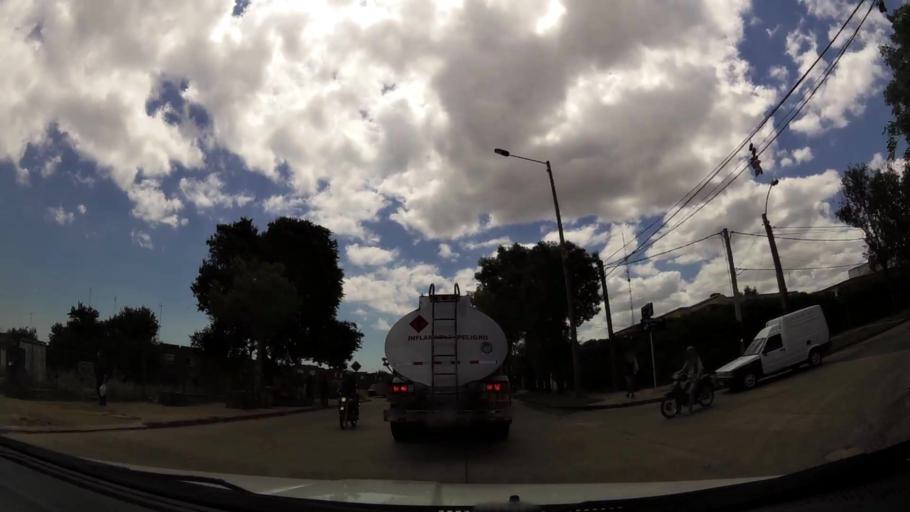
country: UY
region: Canelones
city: La Paz
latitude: -34.8316
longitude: -56.2266
